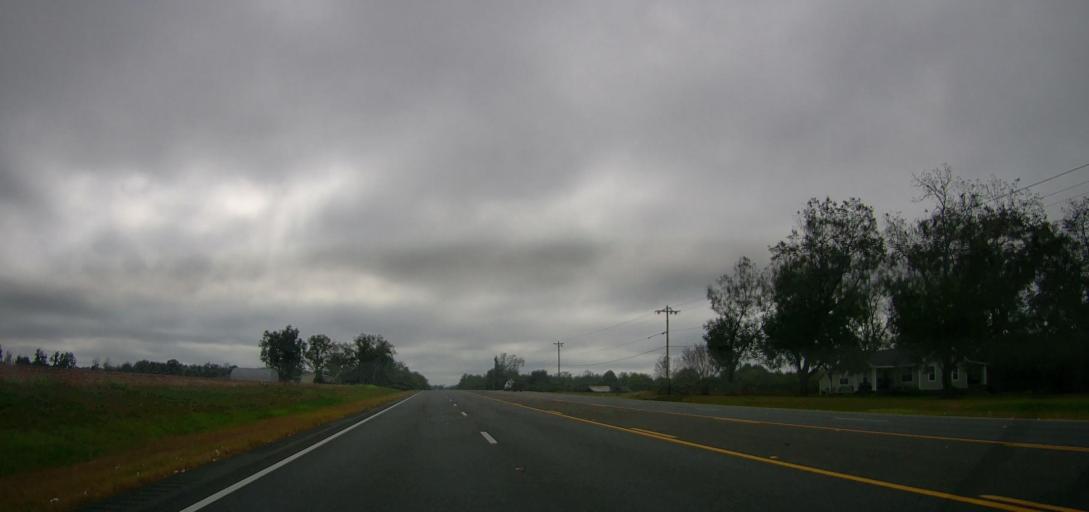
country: US
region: Georgia
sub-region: Thomas County
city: Thomasville
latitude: 30.9656
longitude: -83.8924
